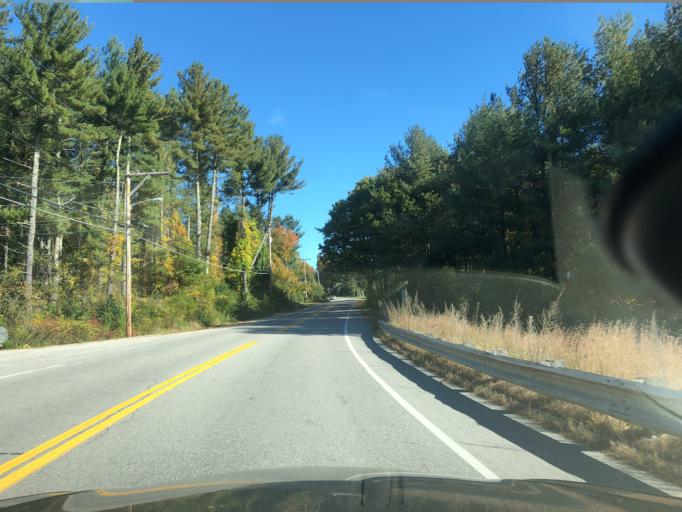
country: US
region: New Hampshire
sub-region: Rockingham County
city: Exeter
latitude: 43.0056
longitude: -70.9474
